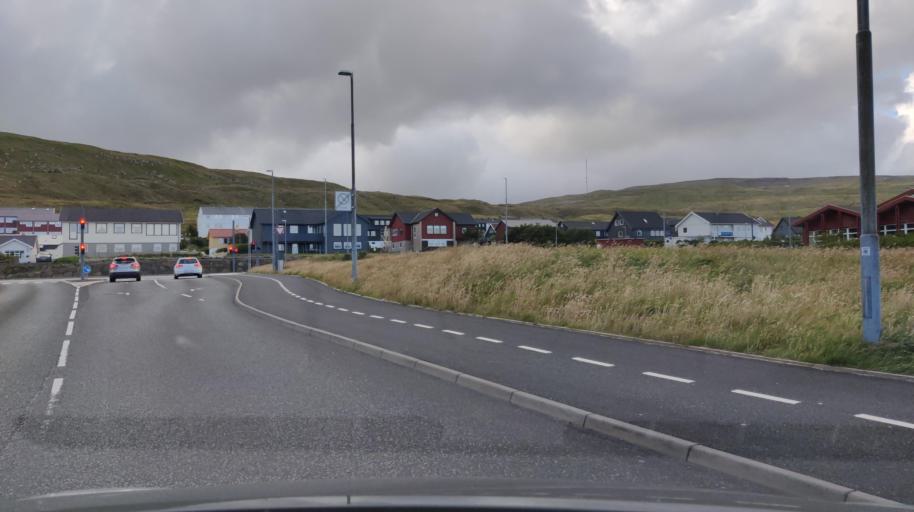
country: FO
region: Streymoy
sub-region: Torshavn
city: Torshavn
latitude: 62.0056
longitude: -6.8009
